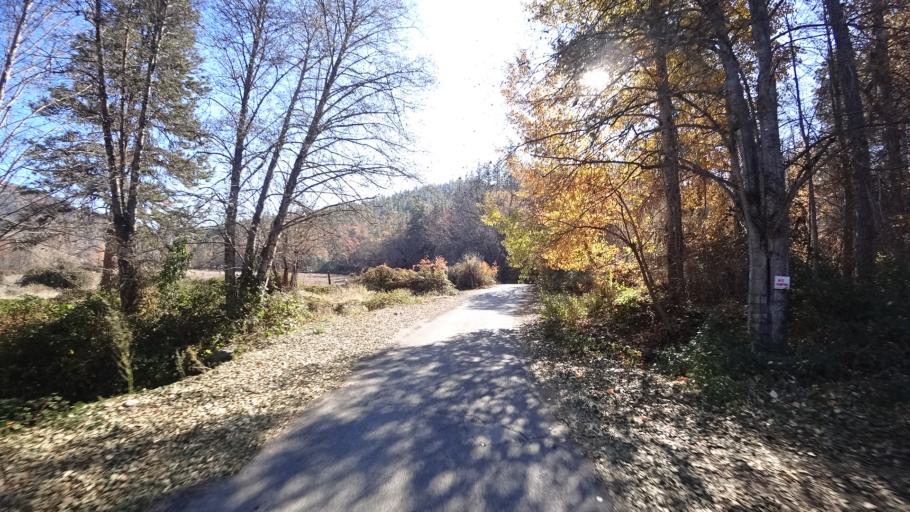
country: US
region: California
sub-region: Siskiyou County
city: Yreka
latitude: 41.8419
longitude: -122.8930
